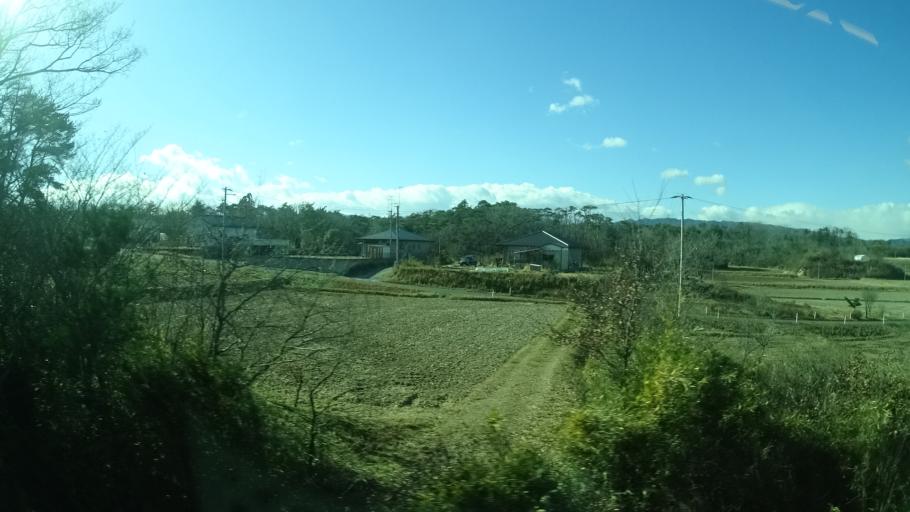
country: JP
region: Miyagi
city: Marumori
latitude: 37.7463
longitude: 140.9420
